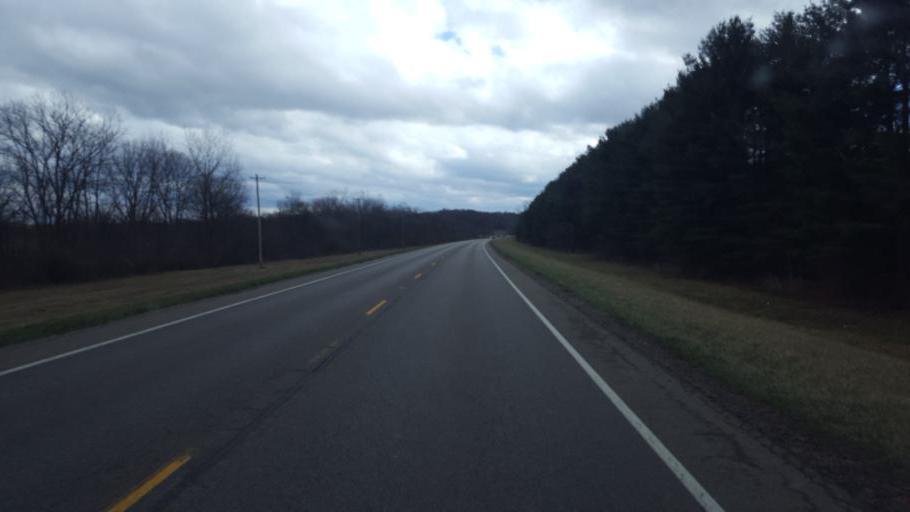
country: US
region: Ohio
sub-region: Muskingum County
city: Frazeysburg
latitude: 40.0575
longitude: -82.1424
